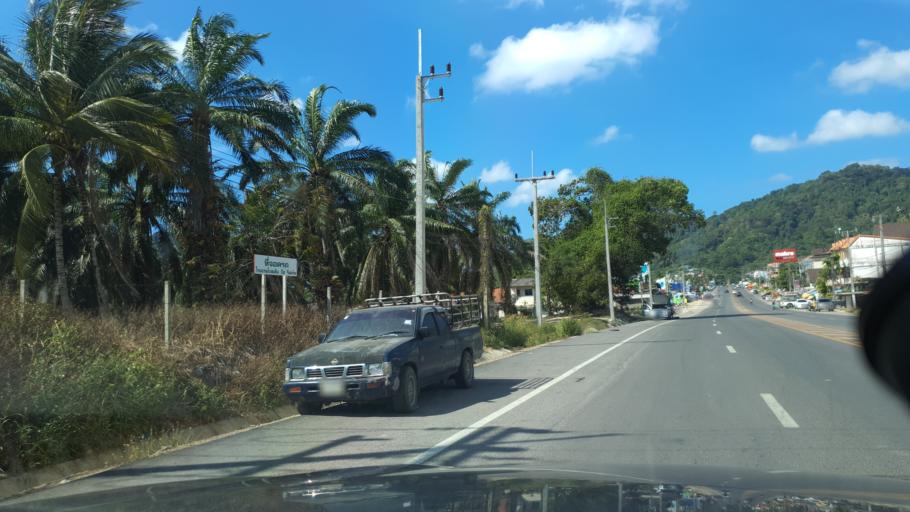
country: TH
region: Phangnga
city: Ban Ao Nang
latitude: 8.0419
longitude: 98.8438
